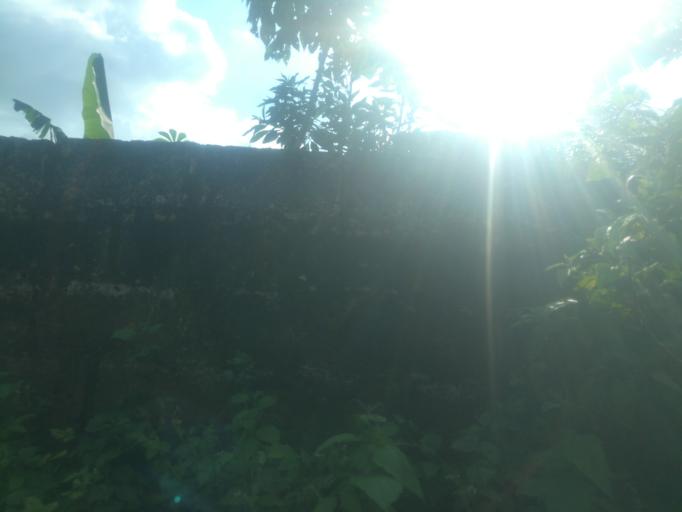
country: NG
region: Oyo
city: Ibadan
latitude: 7.4182
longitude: 3.8355
